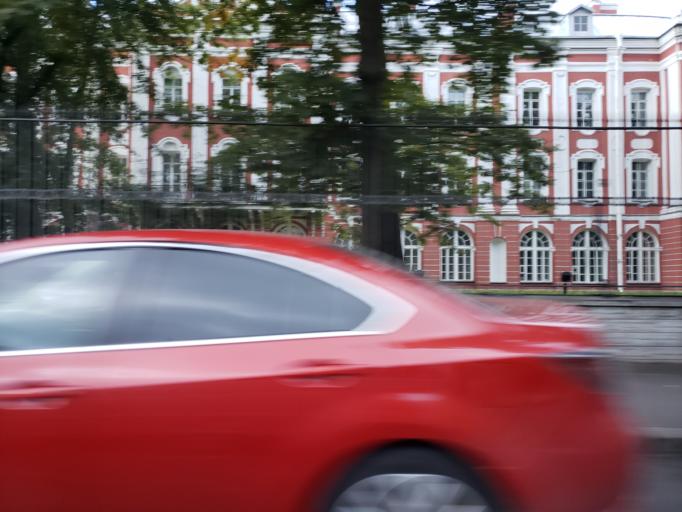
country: RU
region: St.-Petersburg
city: Saint Petersburg
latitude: 59.9421
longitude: 30.2995
